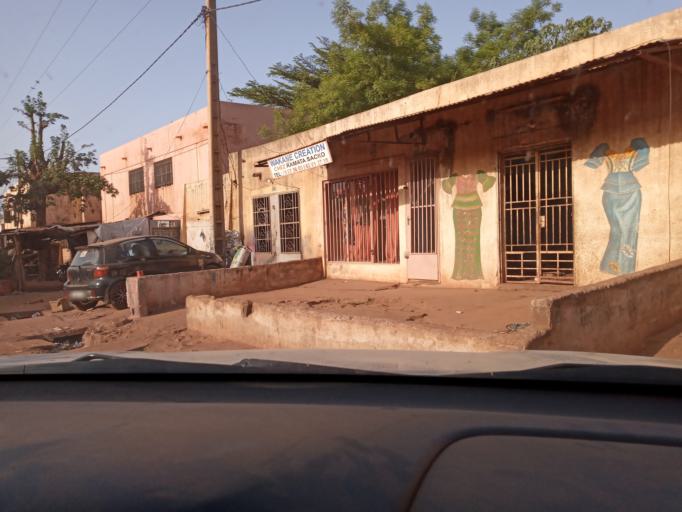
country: ML
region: Bamako
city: Bamako
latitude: 12.6703
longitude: -7.9775
